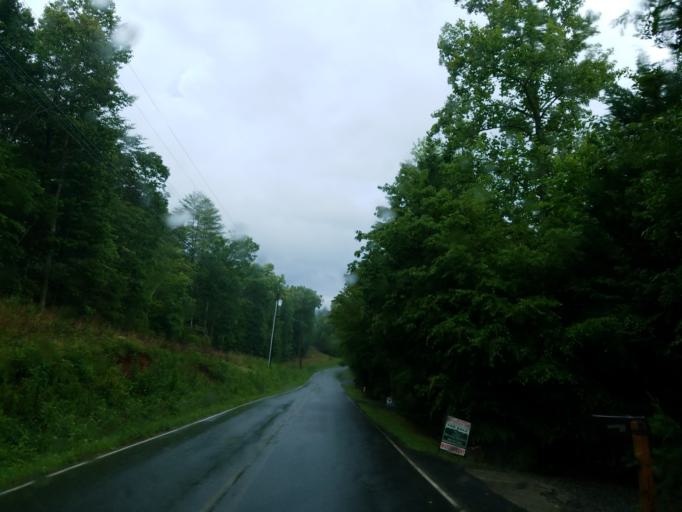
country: US
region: Georgia
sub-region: Fannin County
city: Blue Ridge
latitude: 34.7580
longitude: -84.2096
